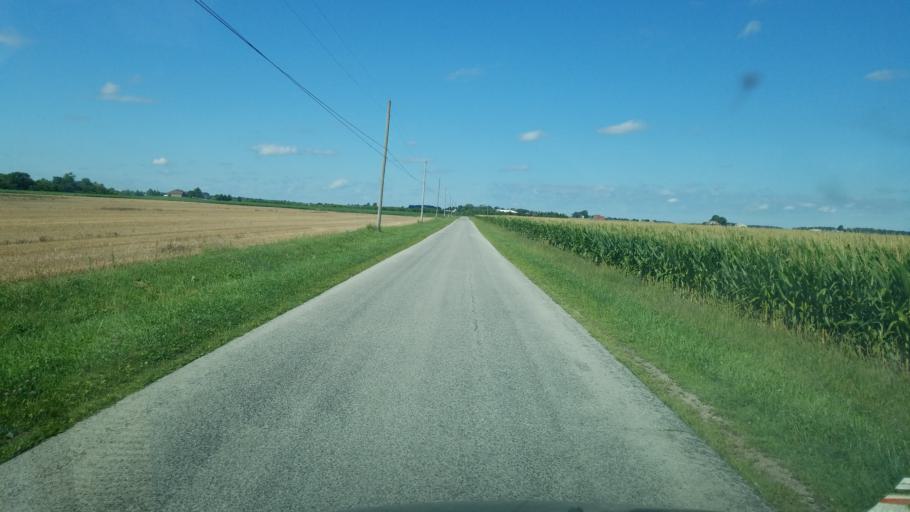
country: US
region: Ohio
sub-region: Hancock County
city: McComb
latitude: 41.1243
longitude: -83.7306
